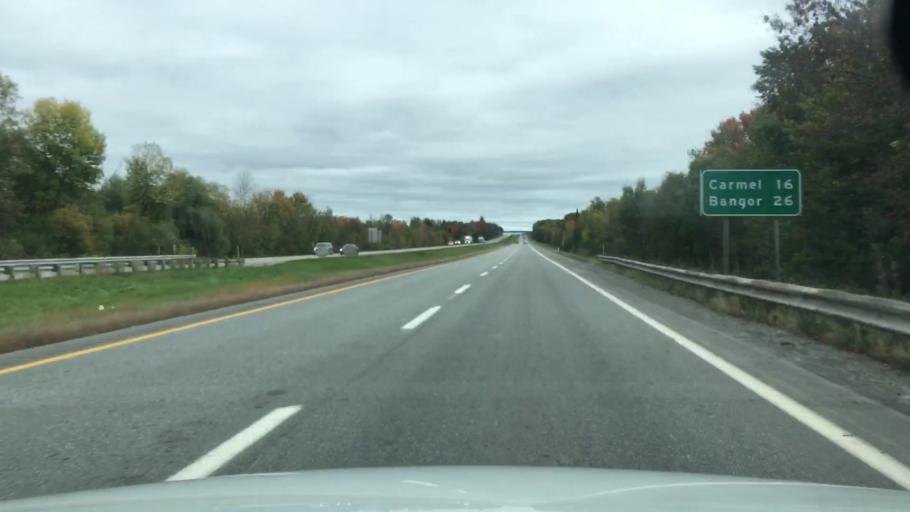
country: US
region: Maine
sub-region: Penobscot County
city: Newport
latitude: 44.8252
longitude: -69.2737
